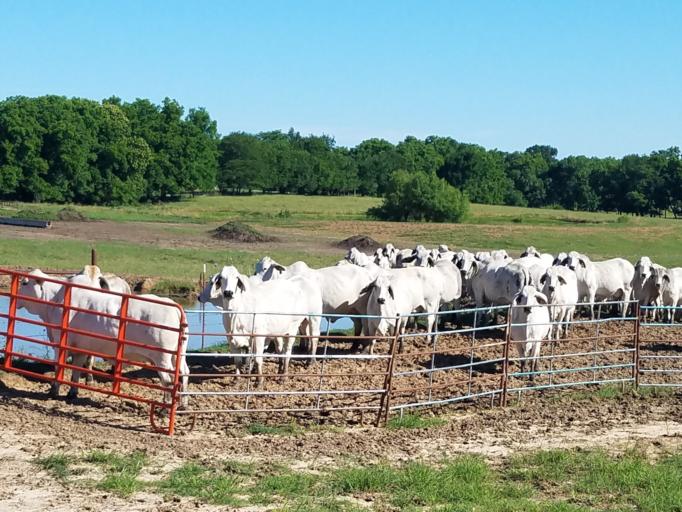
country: US
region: Oklahoma
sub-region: Coal County
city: Coalgate
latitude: 34.4696
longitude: -96.3711
